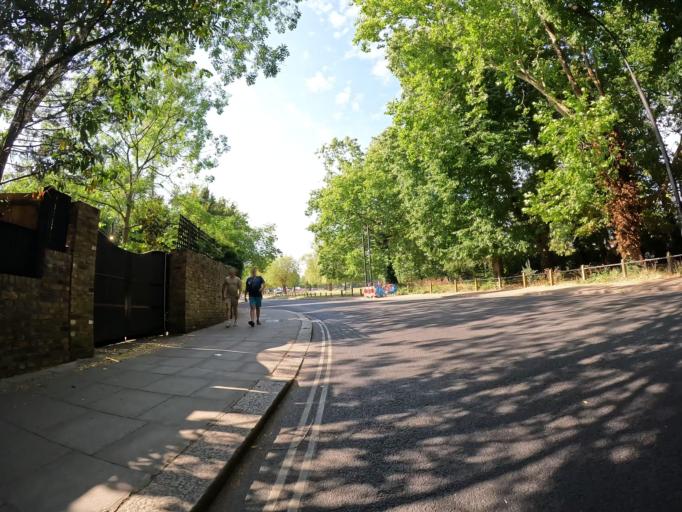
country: GB
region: England
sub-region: Greater London
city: Hadley Wood
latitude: 51.6571
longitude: -0.1754
